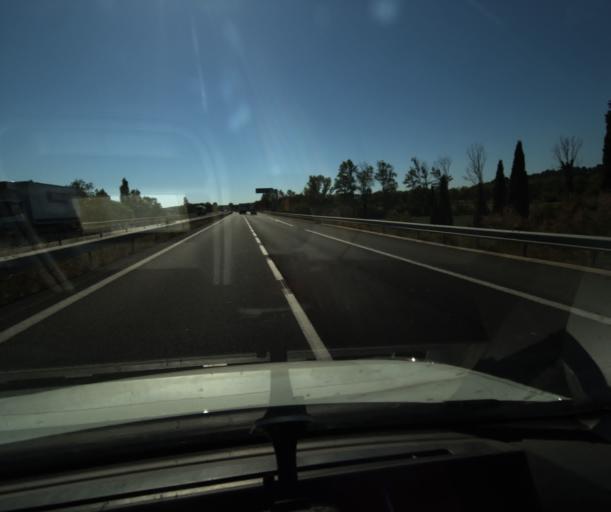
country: FR
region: Languedoc-Roussillon
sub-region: Departement de l'Aude
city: Fabrezan
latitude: 43.1716
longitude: 2.6974
